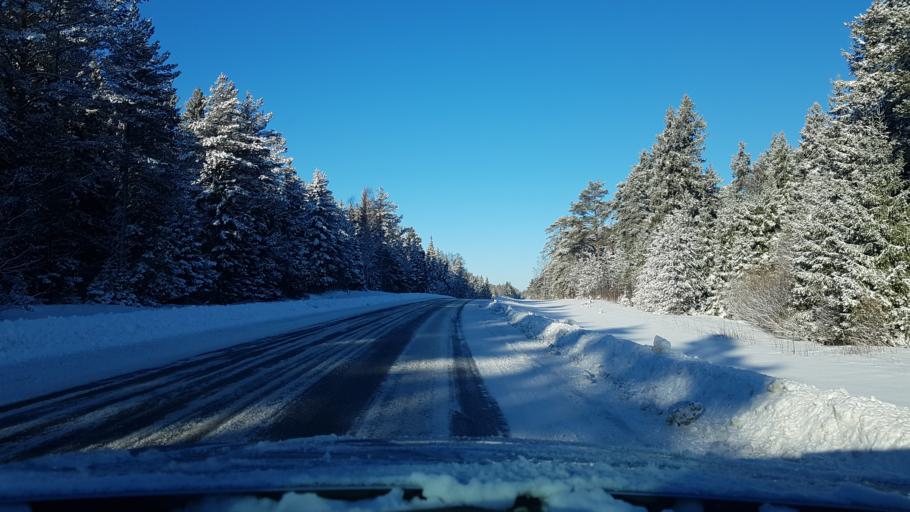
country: EE
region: Hiiumaa
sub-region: Kaerdla linn
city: Kardla
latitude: 58.9656
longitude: 22.8351
